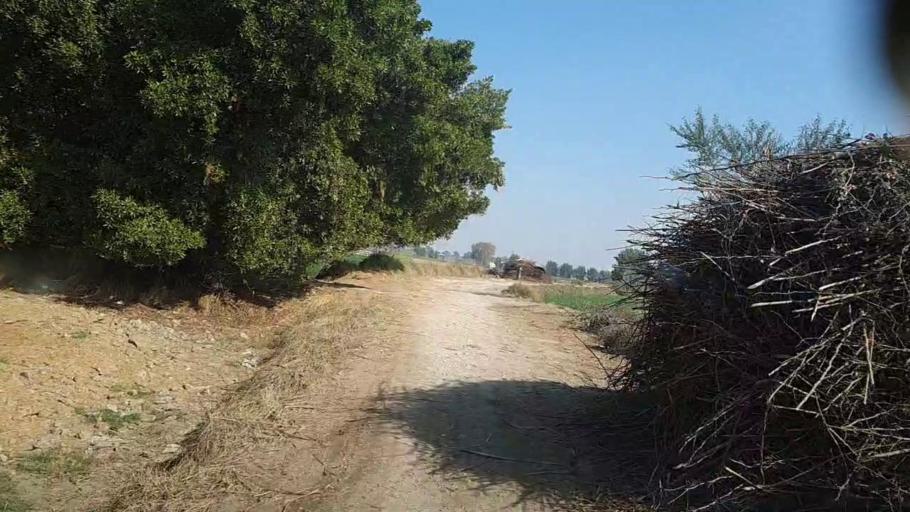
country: PK
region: Sindh
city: Khairpur
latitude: 27.9857
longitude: 69.6884
